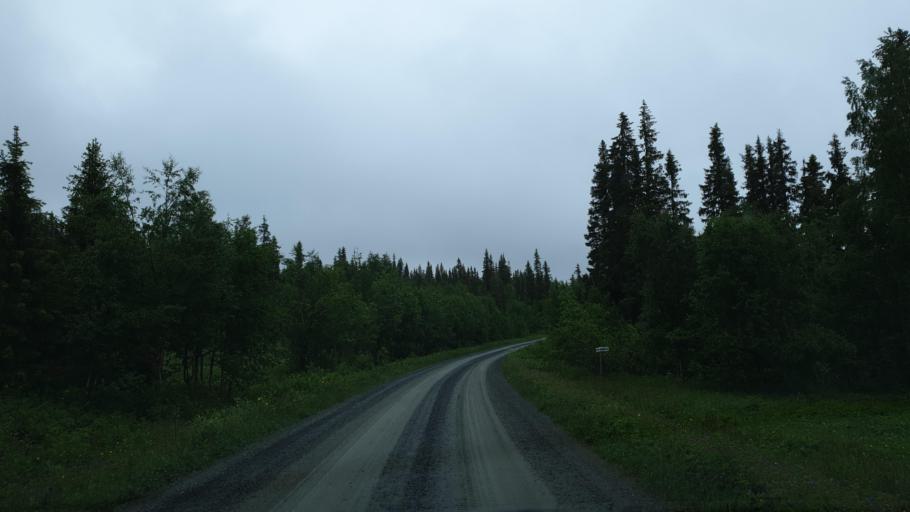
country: SE
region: Vaesterbotten
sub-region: Vilhelmina Kommun
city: Sjoberg
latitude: 65.3271
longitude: 15.9228
